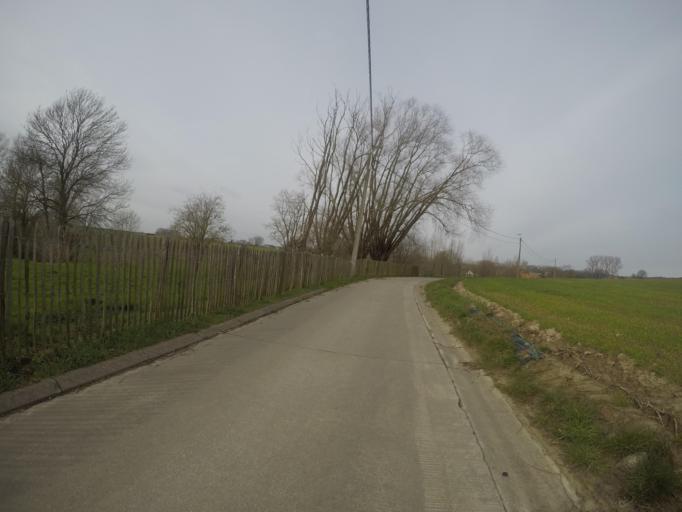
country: BE
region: Flanders
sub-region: Provincie Oost-Vlaanderen
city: Sint-Maria-Lierde
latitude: 50.8260
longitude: 3.8540
